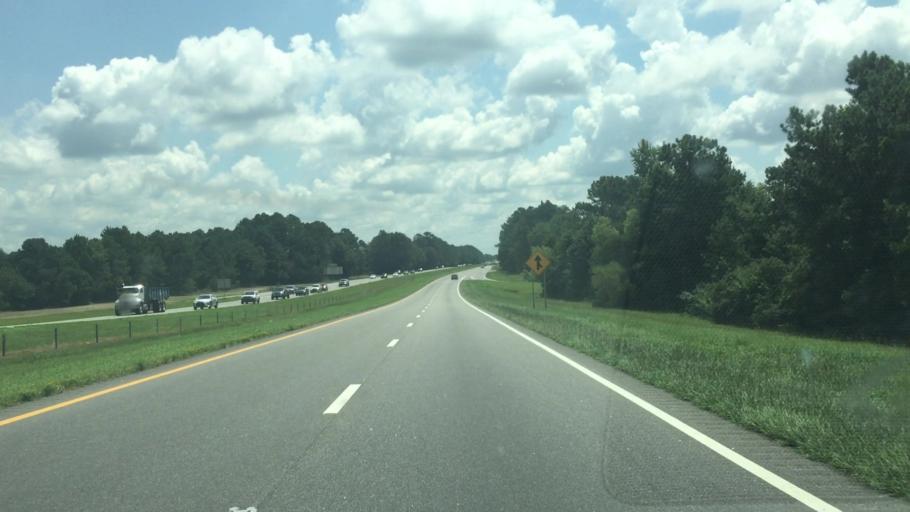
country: US
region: North Carolina
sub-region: Robeson County
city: Maxton
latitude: 34.7570
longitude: -79.3672
